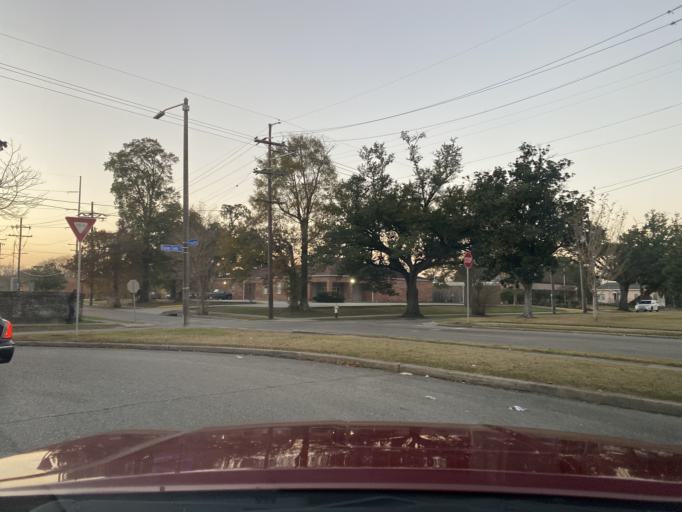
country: US
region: Louisiana
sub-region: Orleans Parish
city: New Orleans
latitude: 30.0008
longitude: -90.0593
